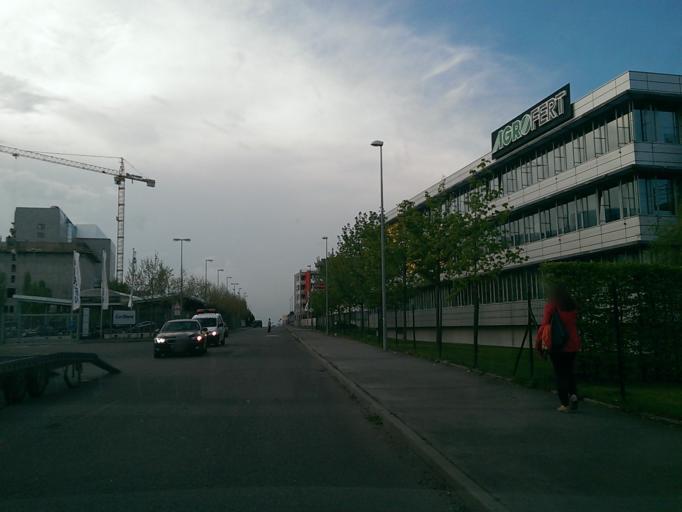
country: CZ
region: Central Bohemia
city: Vestec
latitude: 50.0381
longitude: 14.4976
